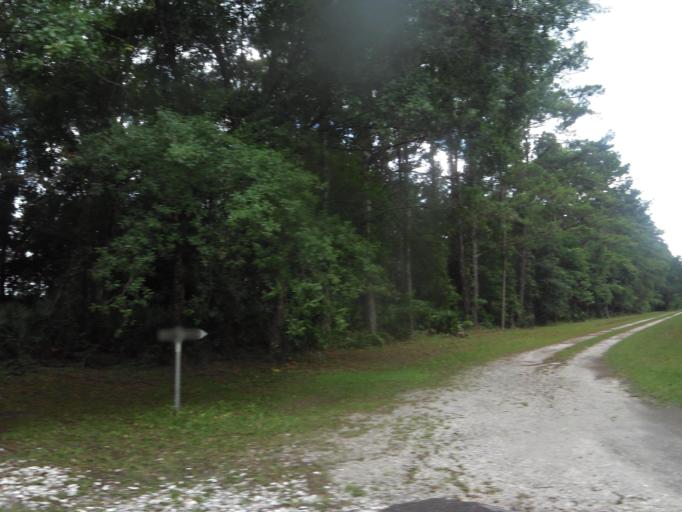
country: US
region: Florida
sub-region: Duval County
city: Baldwin
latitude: 30.3376
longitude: -81.8780
